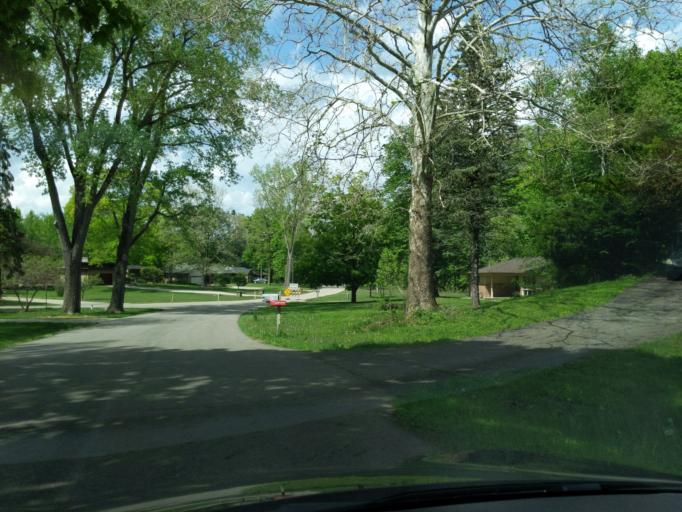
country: US
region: Michigan
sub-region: Ingham County
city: Okemos
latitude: 42.7185
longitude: -84.4392
